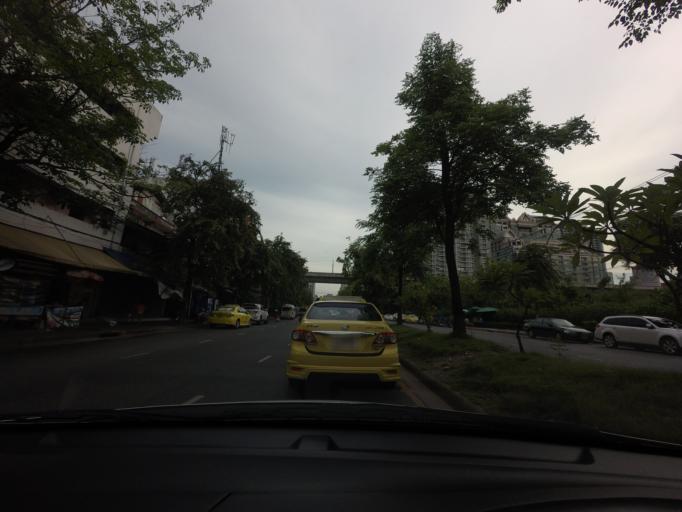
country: TH
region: Bangkok
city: Din Daeng
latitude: 13.7503
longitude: 100.5689
